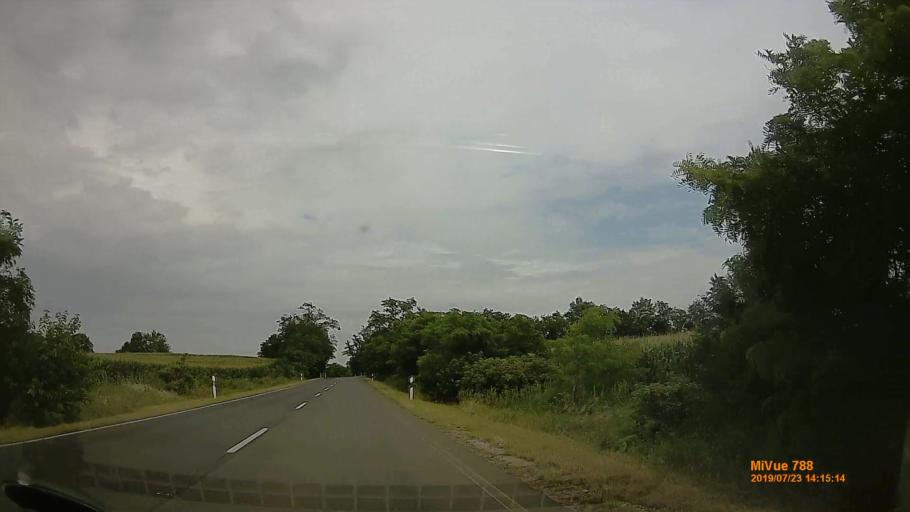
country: HU
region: Szabolcs-Szatmar-Bereg
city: Nagycserkesz
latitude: 47.9578
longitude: 21.5093
